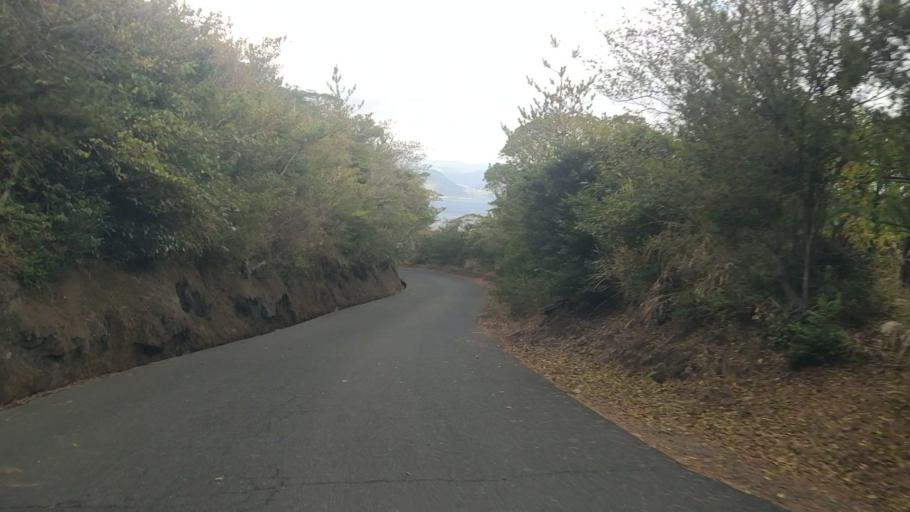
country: JP
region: Kagoshima
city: Kagoshima-shi
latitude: 31.5934
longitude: 130.6352
